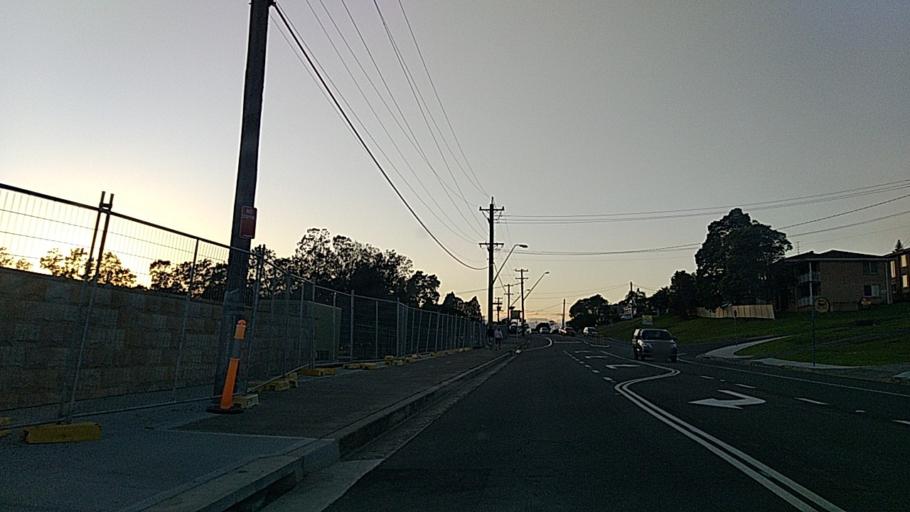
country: AU
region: New South Wales
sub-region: Wollongong
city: Koonawarra
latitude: -34.4907
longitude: 150.8127
